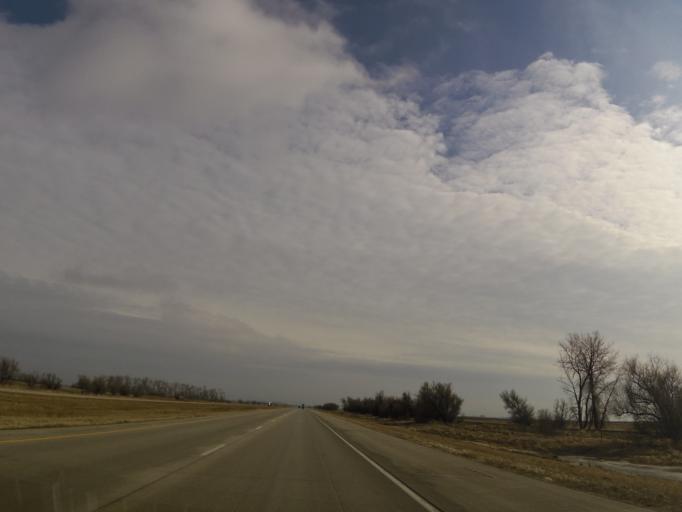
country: US
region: North Dakota
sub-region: Grand Forks County
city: Grand Forks
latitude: 48.0510
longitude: -97.1529
